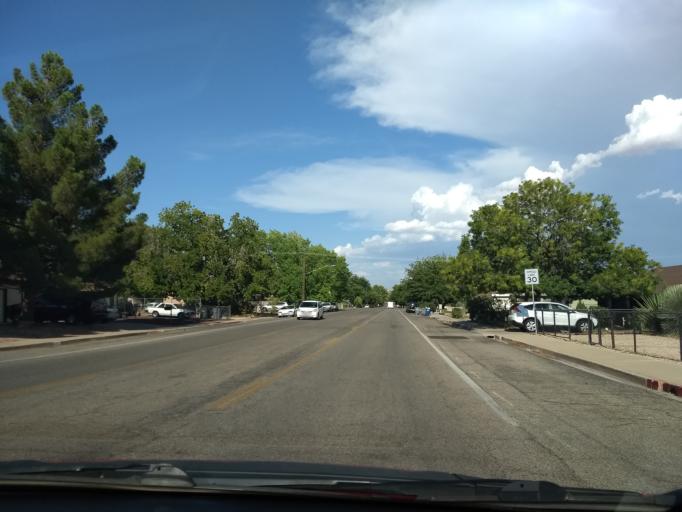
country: US
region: Utah
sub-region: Washington County
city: Saint George
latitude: 37.1065
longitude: -113.5918
